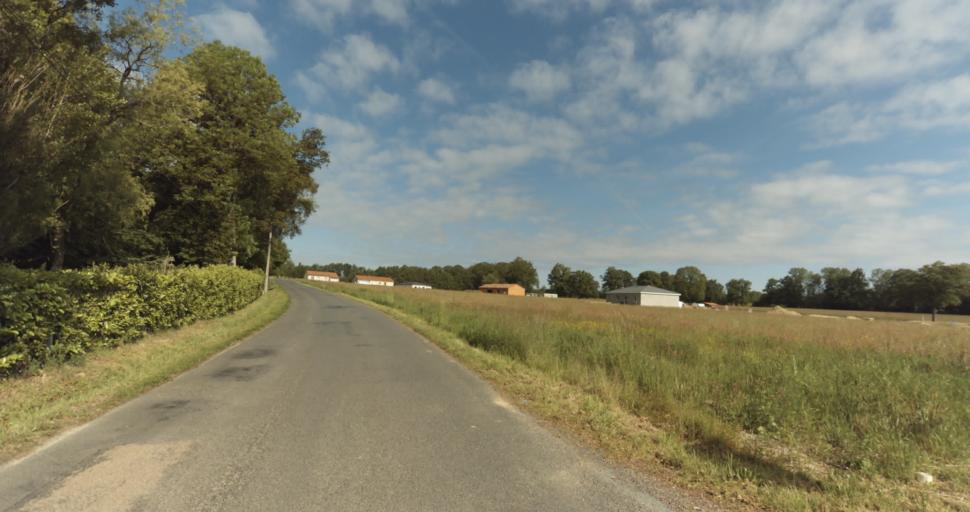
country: FR
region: Limousin
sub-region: Departement de la Haute-Vienne
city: Bosmie-l'Aiguille
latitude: 45.7086
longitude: 1.2396
